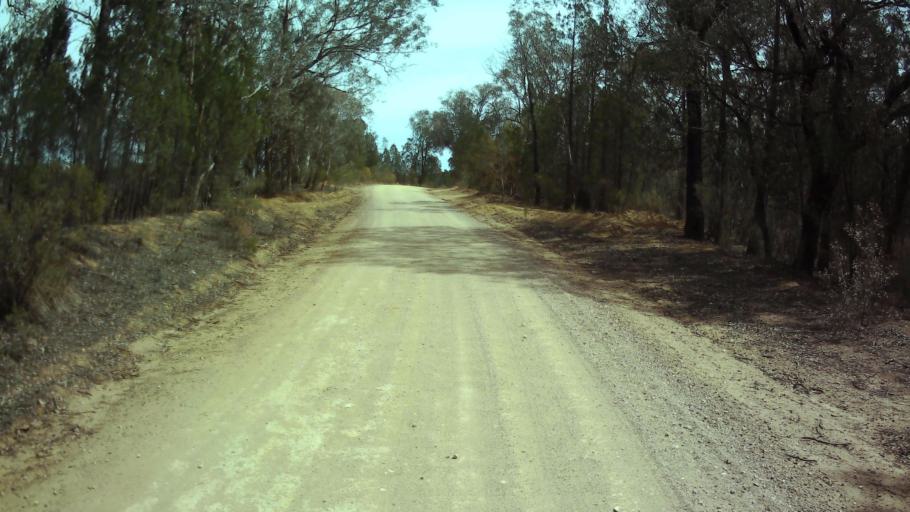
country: AU
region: New South Wales
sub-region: Weddin
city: Grenfell
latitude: -33.9171
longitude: 148.4127
